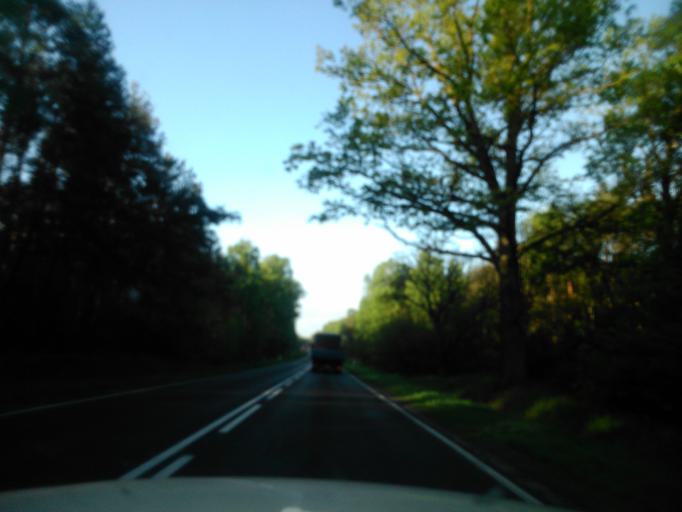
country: PL
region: Masovian Voivodeship
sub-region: Powiat sochaczewski
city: Mlodzieszyn
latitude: 52.3269
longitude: 20.2124
